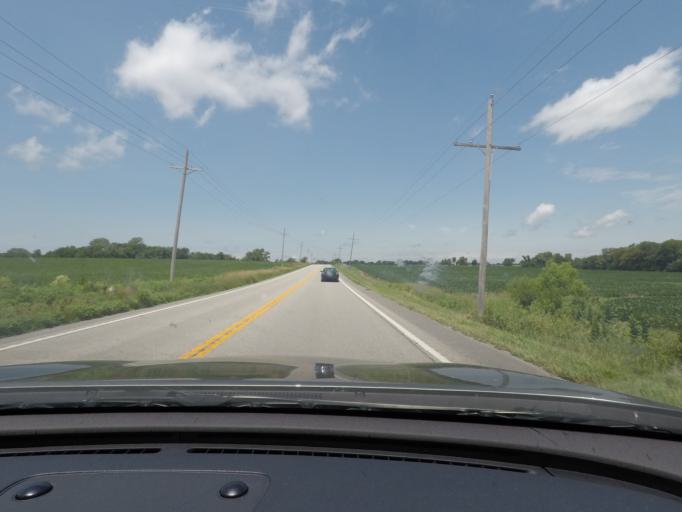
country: US
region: Missouri
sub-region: Saline County
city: Marshall
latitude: 39.1665
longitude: -93.2847
